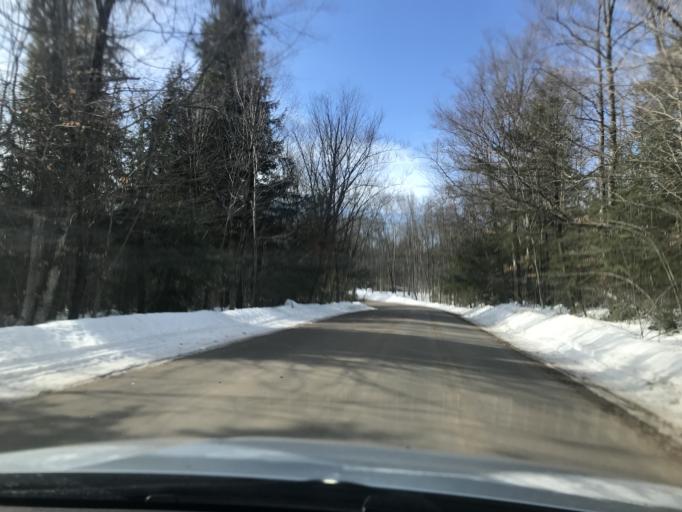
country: US
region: Wisconsin
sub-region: Menominee County
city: Legend Lake
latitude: 45.1238
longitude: -88.4256
